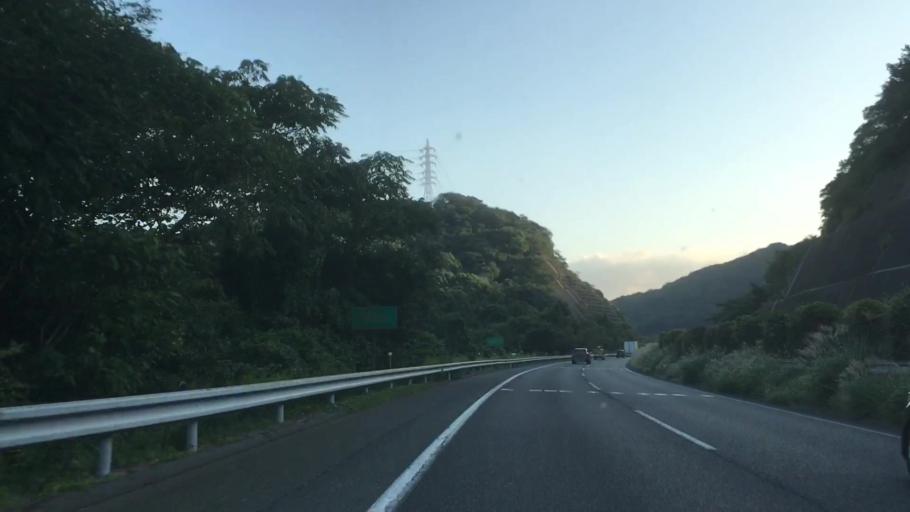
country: JP
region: Yamaguchi
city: Shimonoseki
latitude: 33.8945
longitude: 130.9722
